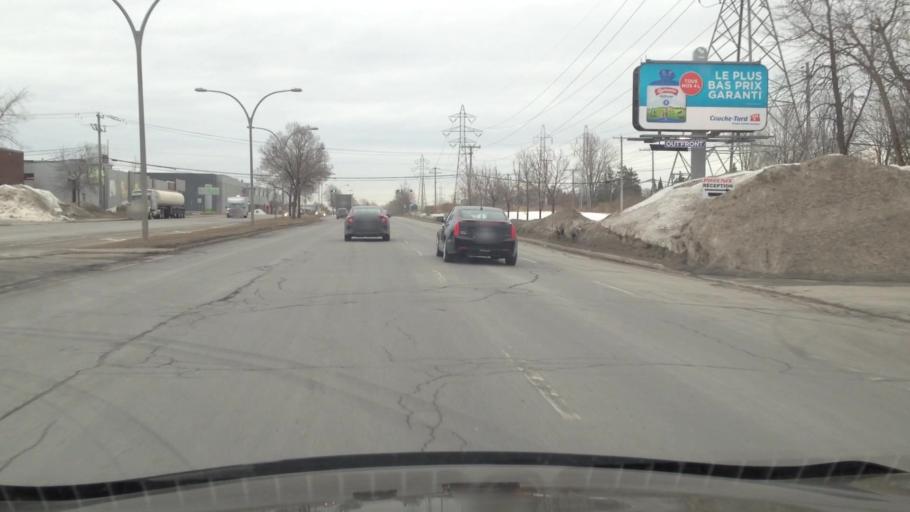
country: CA
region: Quebec
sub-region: Laval
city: Laval
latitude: 45.5809
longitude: -73.7315
